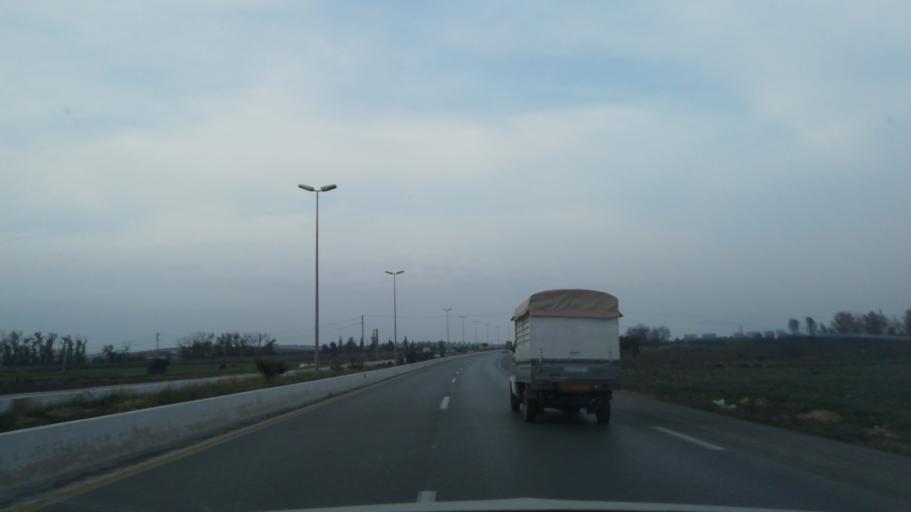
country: DZ
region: Sidi Bel Abbes
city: Sidi Bel Abbes
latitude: 35.1904
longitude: -0.6617
